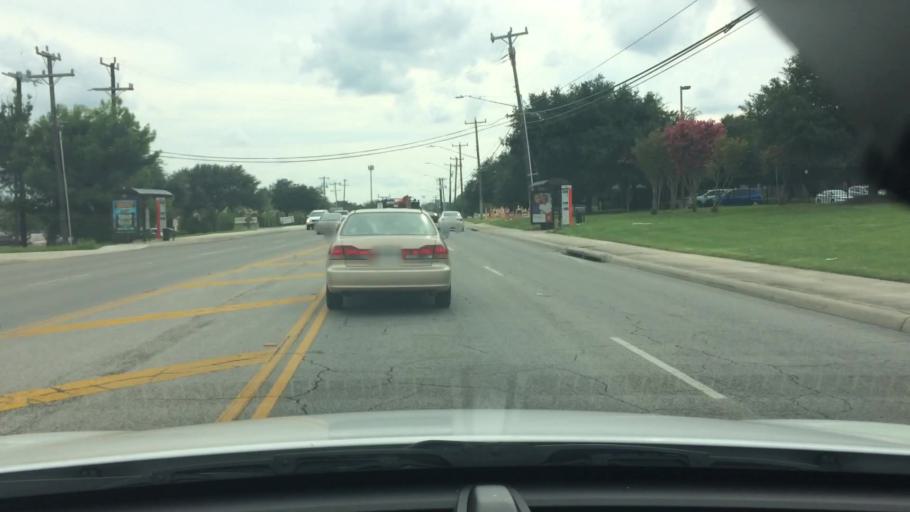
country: US
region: Texas
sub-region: Bexar County
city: Leon Valley
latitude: 29.5181
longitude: -98.6055
